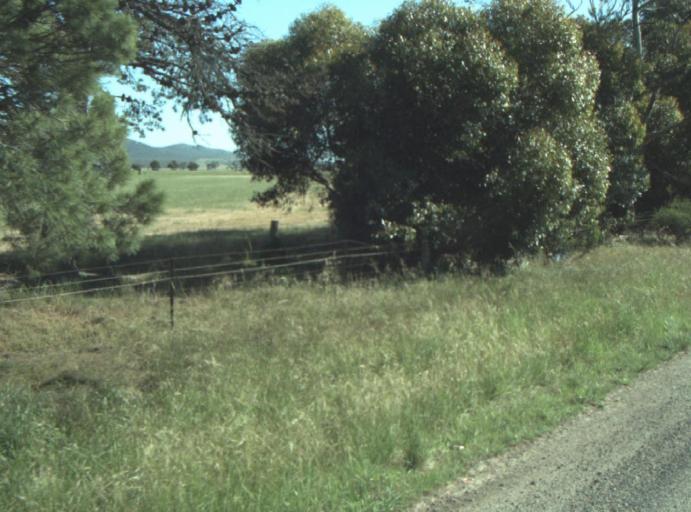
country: AU
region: Victoria
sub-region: Greater Geelong
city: Lara
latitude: -37.9989
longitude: 144.4440
